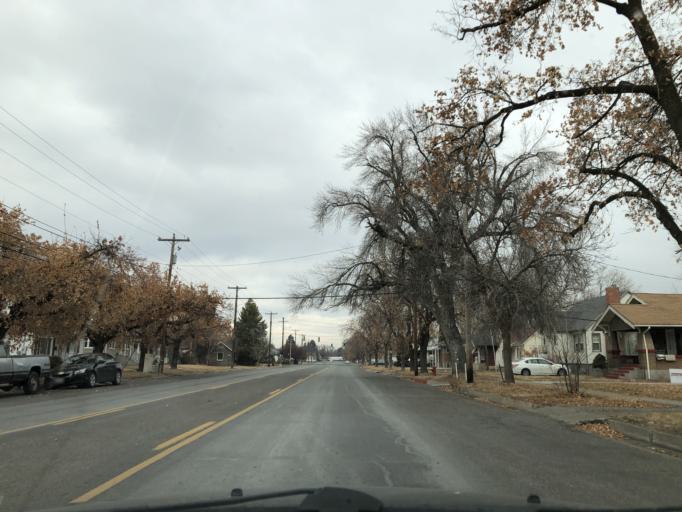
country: US
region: Utah
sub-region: Cache County
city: Logan
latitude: 41.7377
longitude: -111.8374
